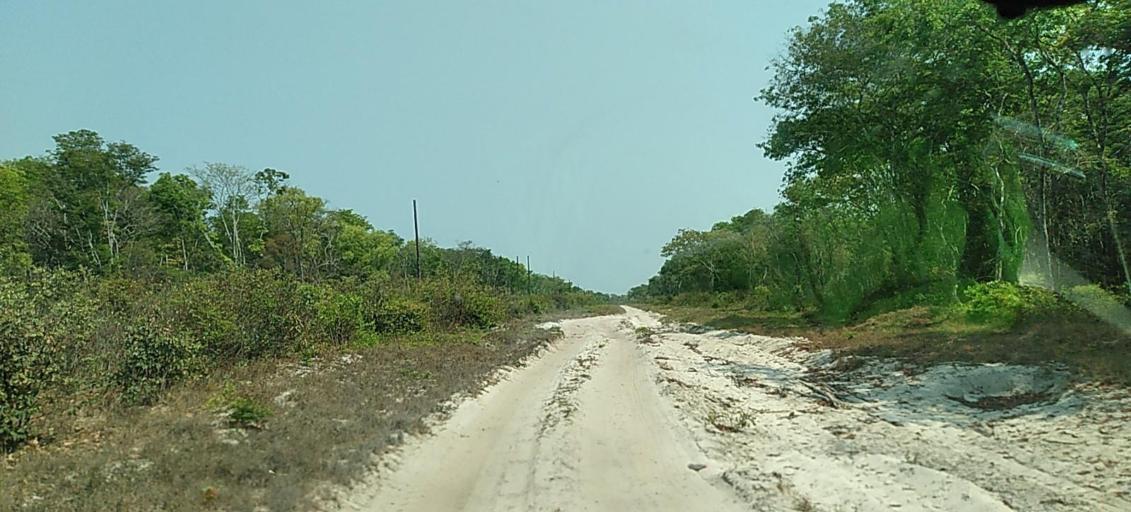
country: ZM
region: North-Western
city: Kabompo
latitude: -13.2653
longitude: 24.0520
